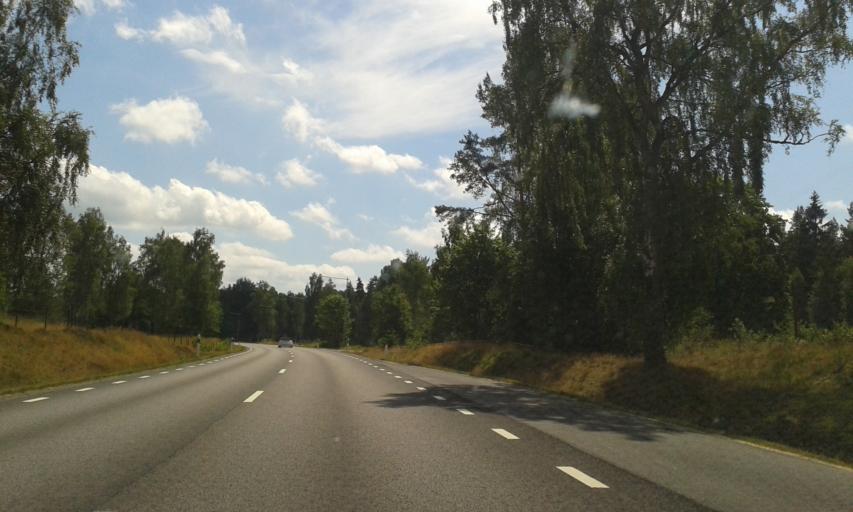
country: SE
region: Kronoberg
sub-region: Alvesta Kommun
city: Vislanda
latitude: 56.9110
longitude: 14.4261
